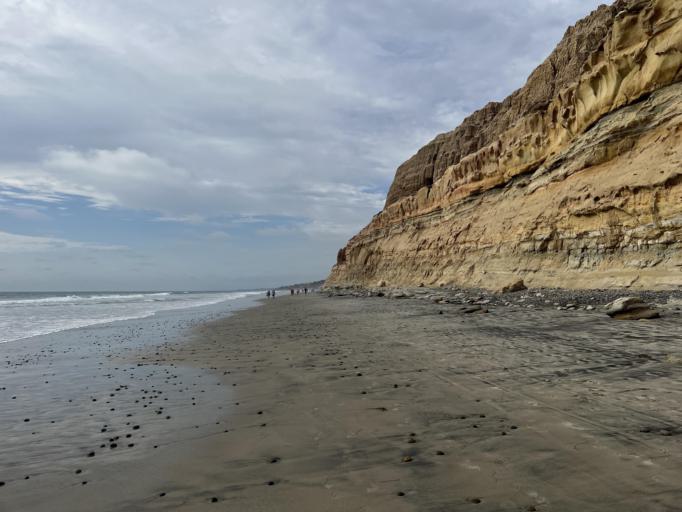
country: US
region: California
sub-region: San Diego County
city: Del Mar
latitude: 32.9153
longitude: -117.2587
